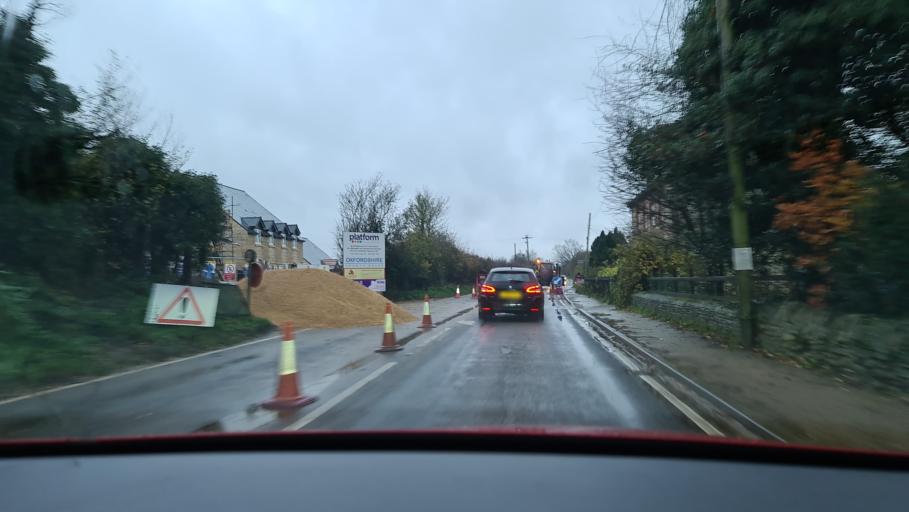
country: GB
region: England
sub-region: Oxfordshire
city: Somerton
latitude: 51.9414
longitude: -1.2121
